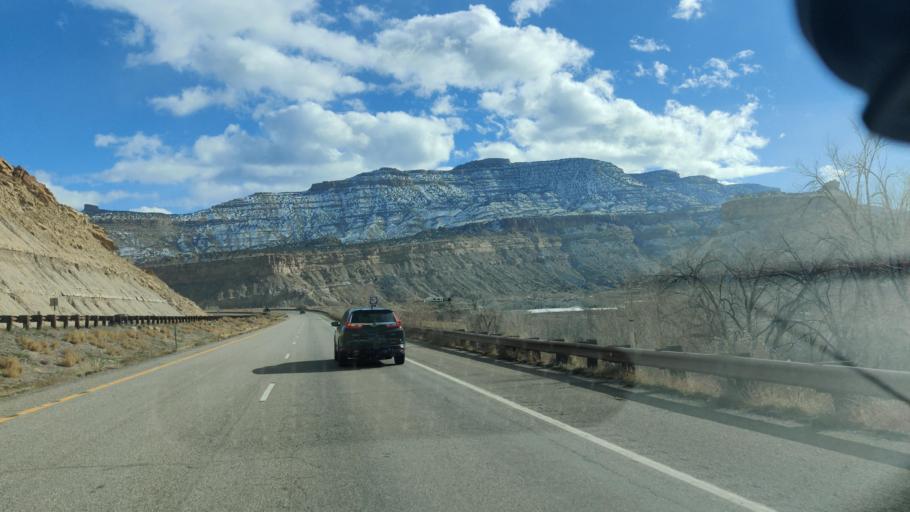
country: US
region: Colorado
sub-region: Mesa County
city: Palisade
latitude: 39.1198
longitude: -108.3367
